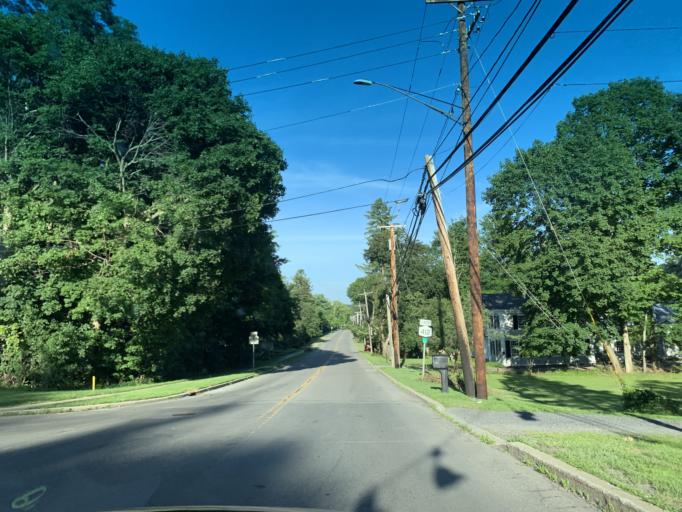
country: US
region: New York
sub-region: Oneida County
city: Clinton
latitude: 43.0485
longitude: -75.3959
